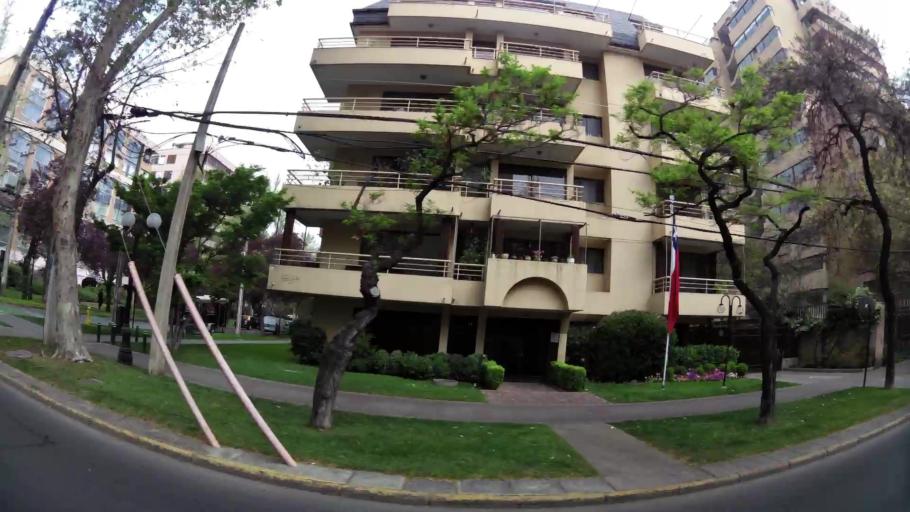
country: CL
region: Santiago Metropolitan
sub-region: Provincia de Santiago
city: Villa Presidente Frei, Nunoa, Santiago, Chile
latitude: -33.4242
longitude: -70.6006
